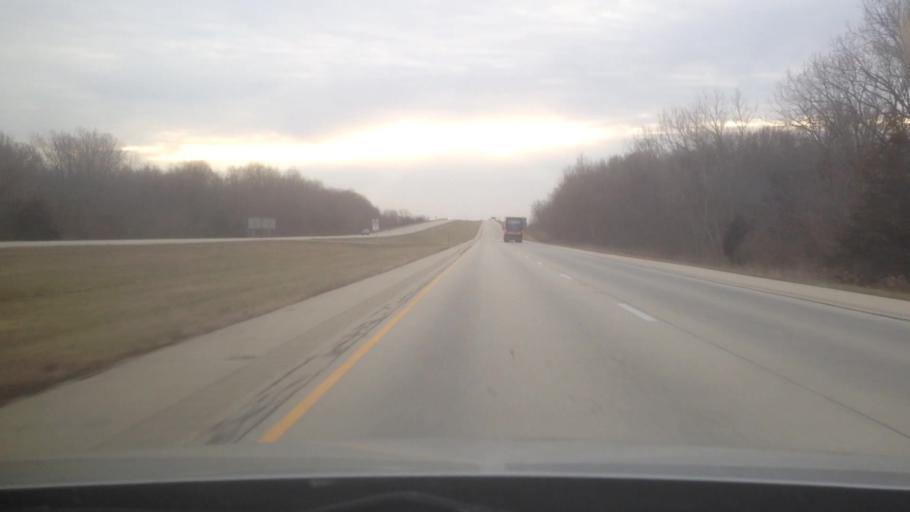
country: US
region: Illinois
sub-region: Macon County
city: Decatur
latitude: 39.8067
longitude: -89.0188
